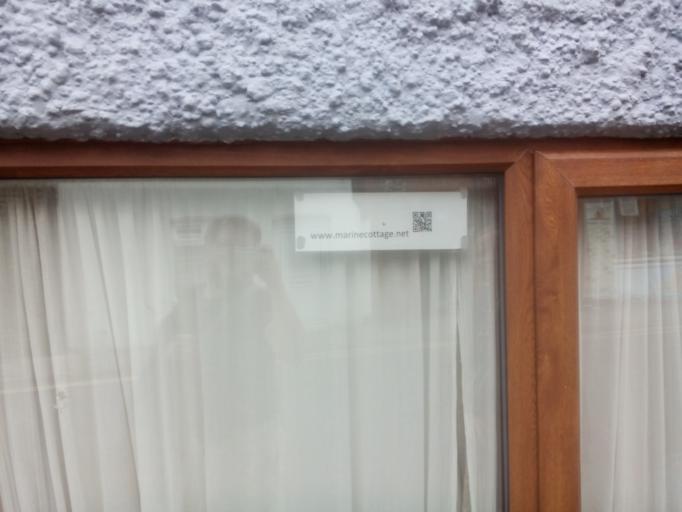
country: GB
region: England
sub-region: Norfolk
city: Sheringham
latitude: 52.9451
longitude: 1.2123
